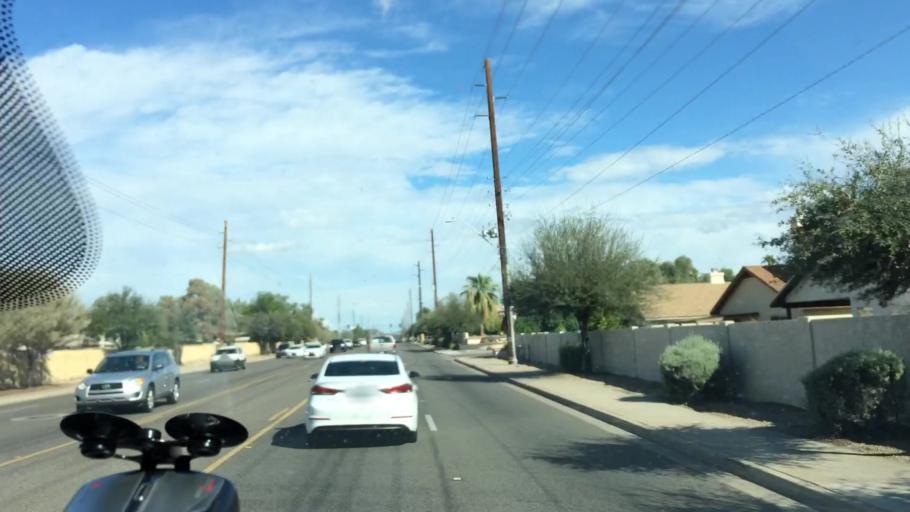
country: US
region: Arizona
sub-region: Maricopa County
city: Glendale
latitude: 33.5672
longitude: -112.1979
